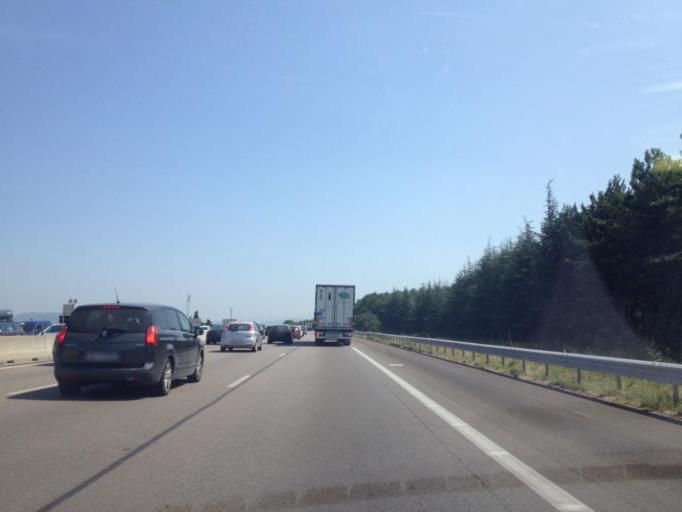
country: FR
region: Rhone-Alpes
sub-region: Departement de la Drome
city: Allan
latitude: 44.5227
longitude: 4.7934
